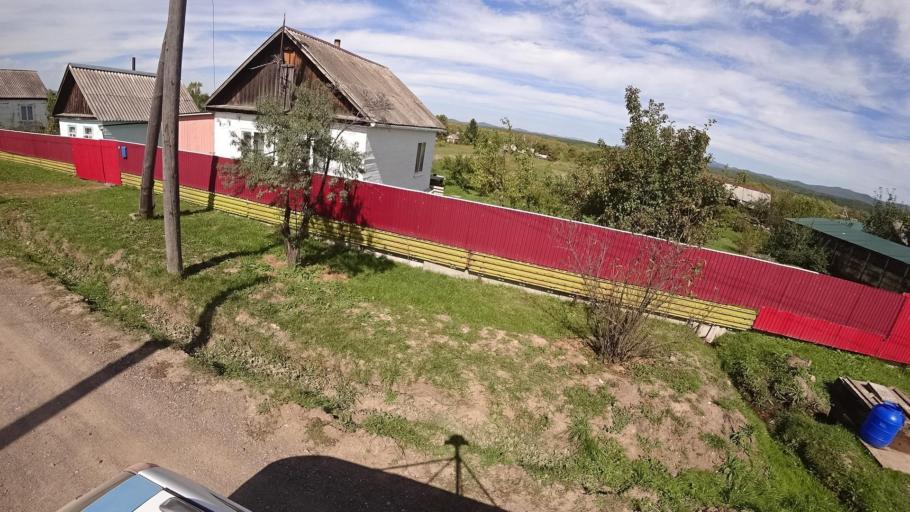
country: RU
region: Primorskiy
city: Yakovlevka
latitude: 44.4324
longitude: 133.5595
